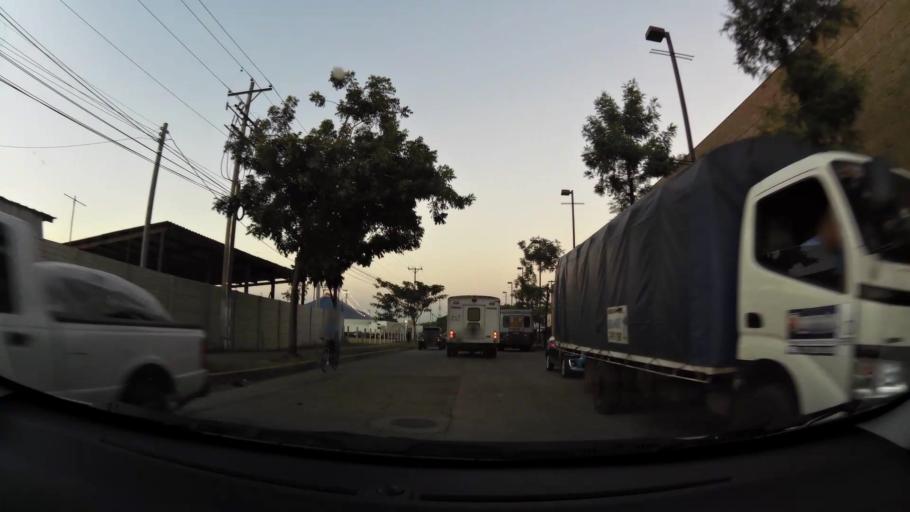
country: SV
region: La Libertad
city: Santa Tecla
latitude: 13.7288
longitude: -89.3601
